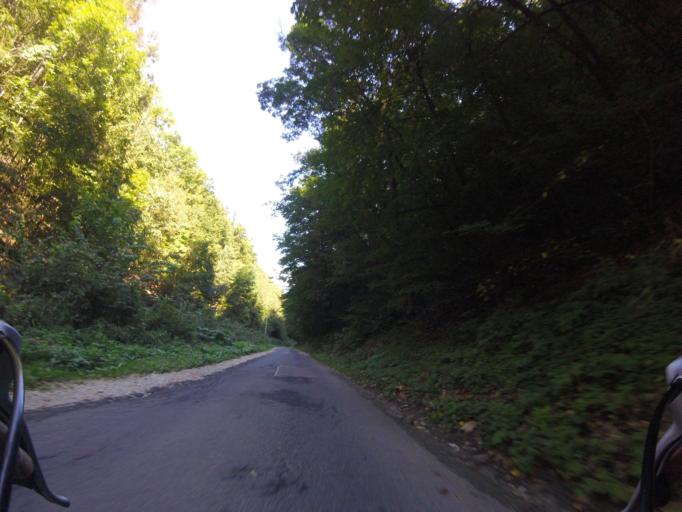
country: HU
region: Heves
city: Szilvasvarad
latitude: 48.1114
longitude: 20.5383
